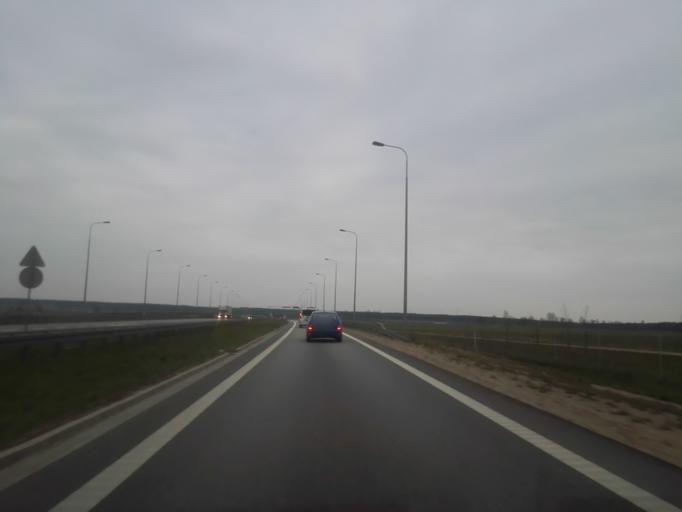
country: PL
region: Podlasie
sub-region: Powiat kolnenski
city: Stawiski
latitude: 53.3929
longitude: 22.1501
